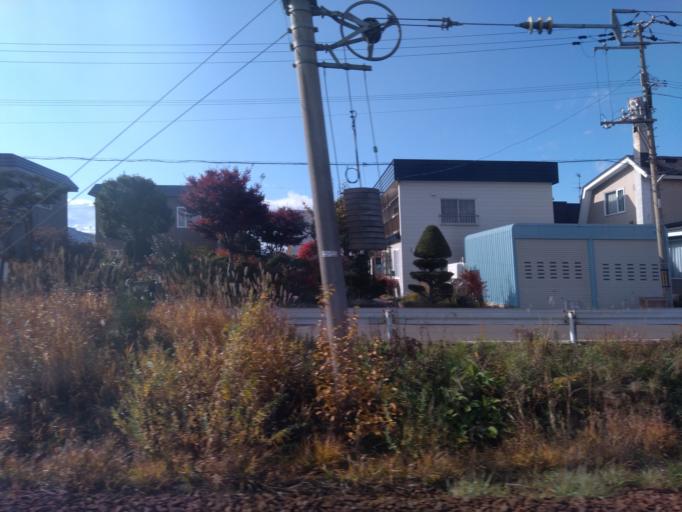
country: JP
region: Hokkaido
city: Kitahiroshima
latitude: 42.9170
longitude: 141.5735
